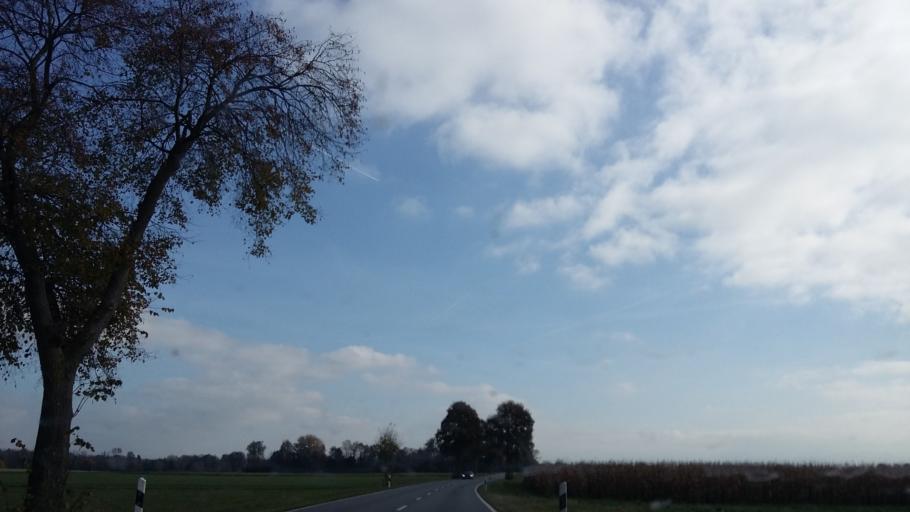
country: DE
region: Bavaria
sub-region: Upper Bavaria
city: Bad Aibling
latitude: 47.8609
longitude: 11.9601
